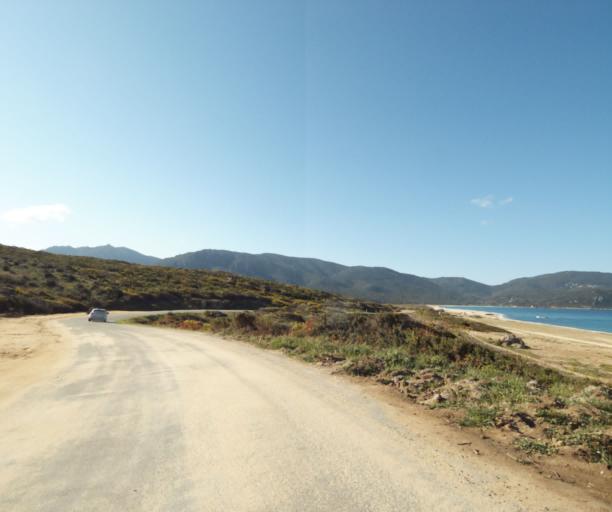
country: FR
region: Corsica
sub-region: Departement de la Corse-du-Sud
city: Propriano
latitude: 41.6691
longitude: 8.8831
